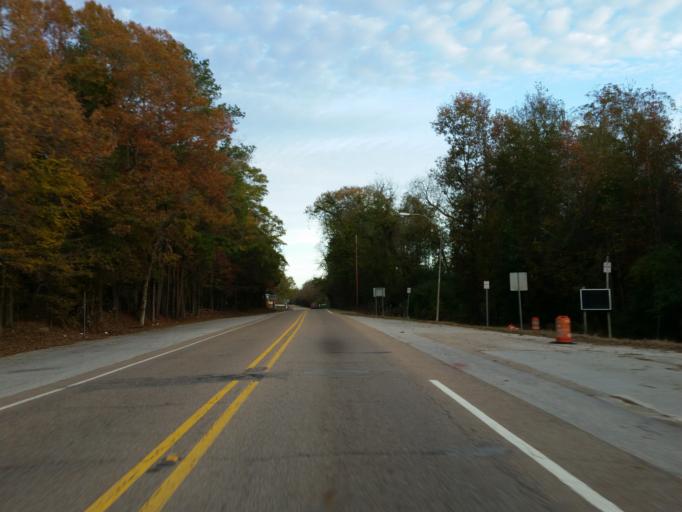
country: US
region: Alabama
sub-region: Sumter County
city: York
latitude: 32.4244
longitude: -88.4413
